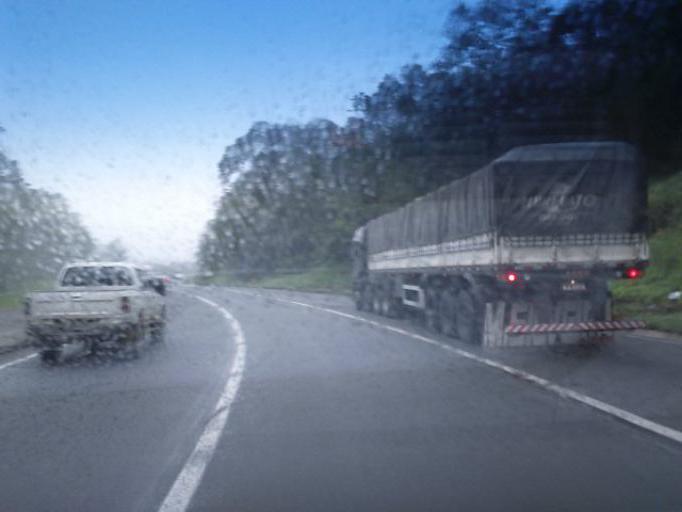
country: BR
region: Parana
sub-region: Guaratuba
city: Guaratuba
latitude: -25.8639
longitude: -48.9507
